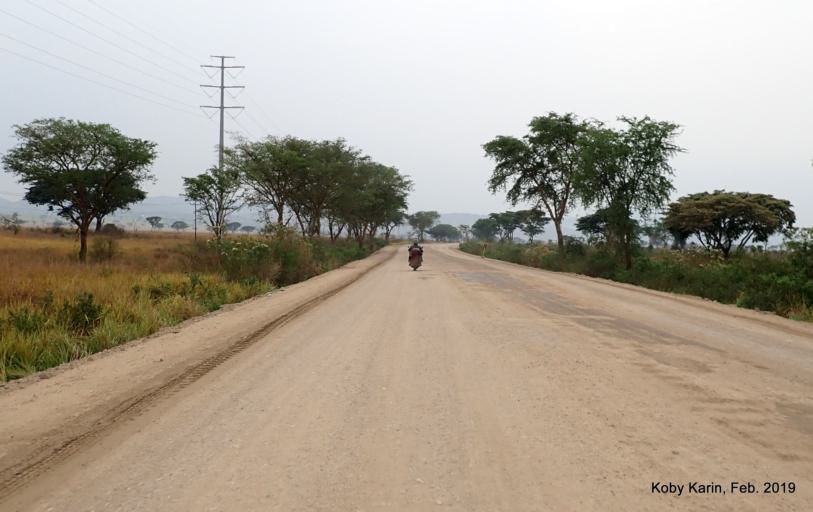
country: UG
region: Western Region
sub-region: Rubirizi District
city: Rubirizi
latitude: -0.1751
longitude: 30.0796
